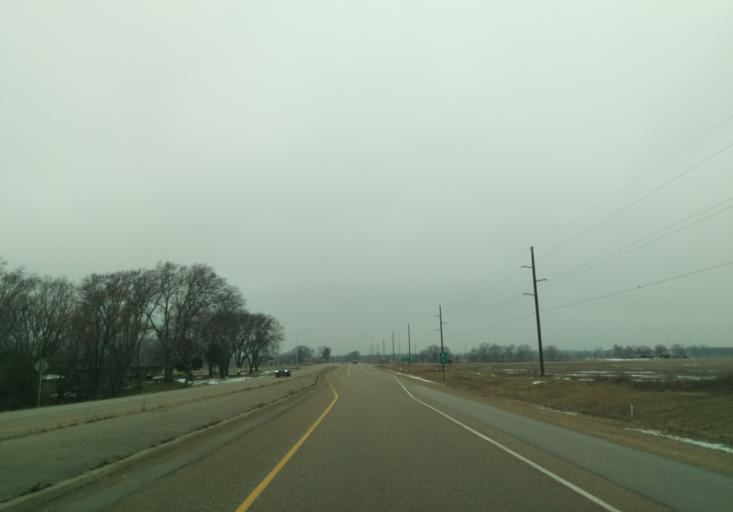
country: US
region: Wisconsin
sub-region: Dane County
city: Mazomanie
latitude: 43.1666
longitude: -89.7714
